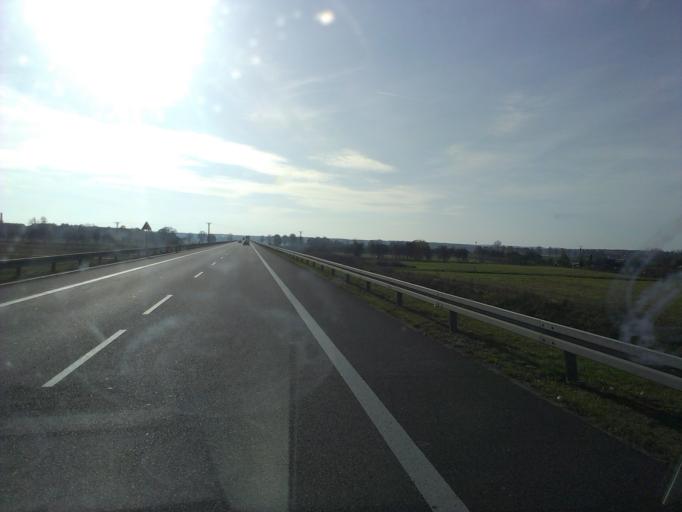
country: PL
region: Lubusz
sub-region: Powiat miedzyrzecki
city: Miedzyrzecz
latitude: 52.4479
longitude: 15.5610
